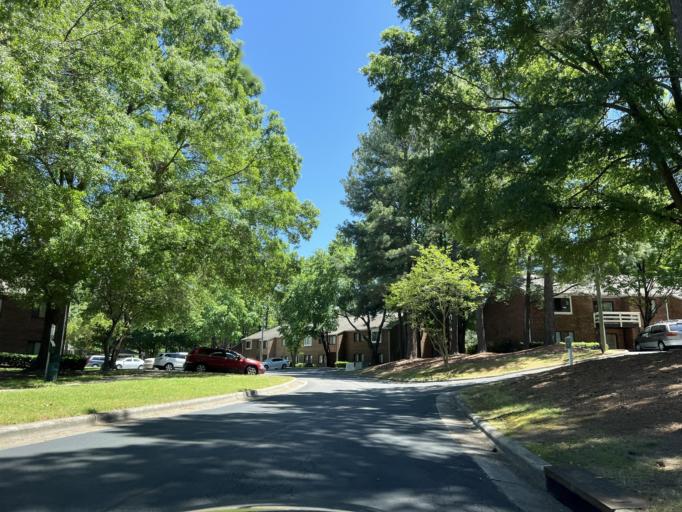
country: US
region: North Carolina
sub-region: Wake County
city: Raleigh
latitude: 35.8544
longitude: -78.5747
